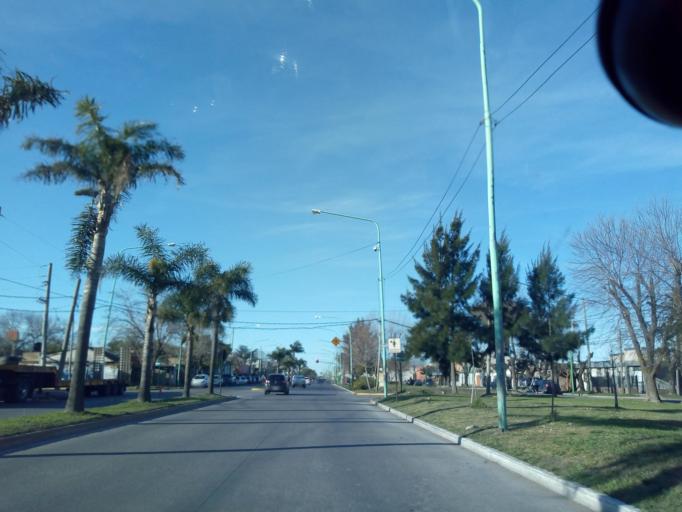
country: AR
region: Buenos Aires
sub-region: Partido de Ensenada
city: Ensenada
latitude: -34.8710
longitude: -57.9119
